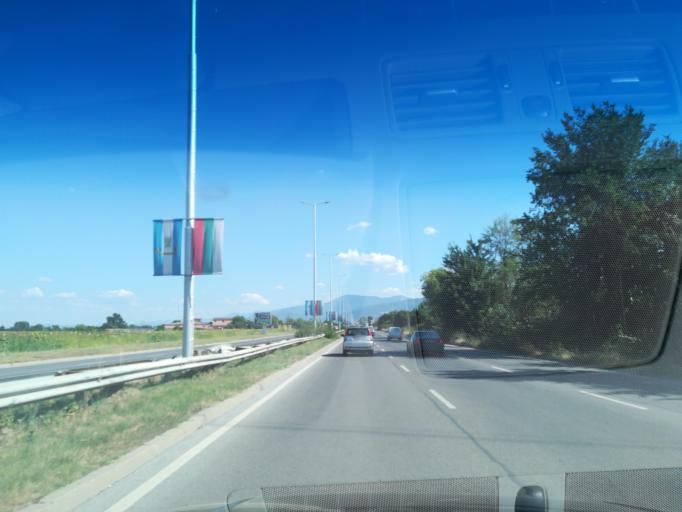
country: BG
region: Plovdiv
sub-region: Obshtina Plovdiv
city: Plovdiv
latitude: 42.1071
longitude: 24.7828
